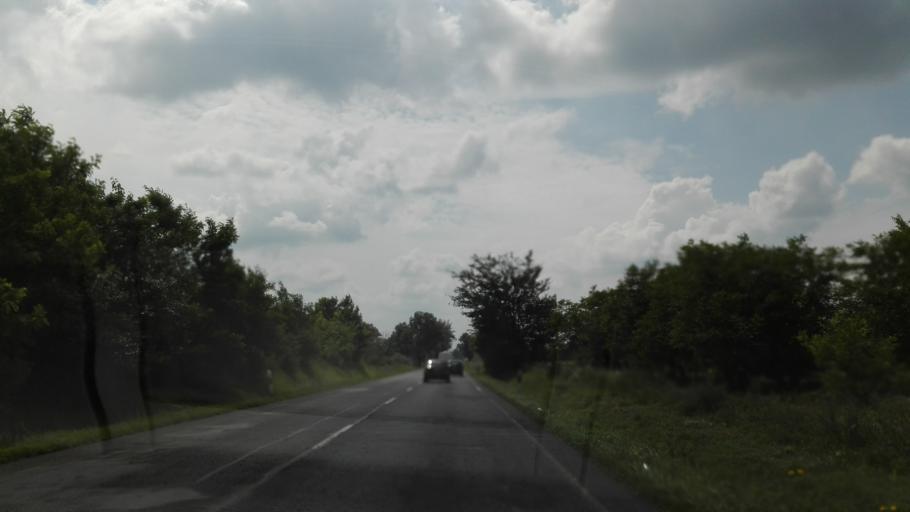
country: HU
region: Fejer
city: Alap
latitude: 46.7962
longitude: 18.7067
